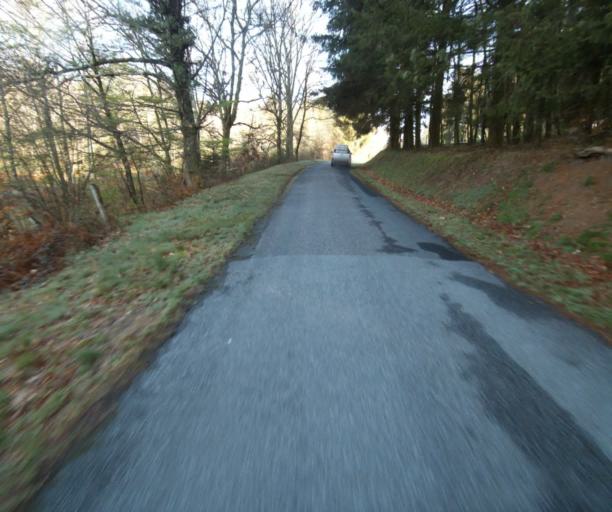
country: FR
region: Limousin
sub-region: Departement de la Correze
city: Correze
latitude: 45.2845
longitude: 1.8662
